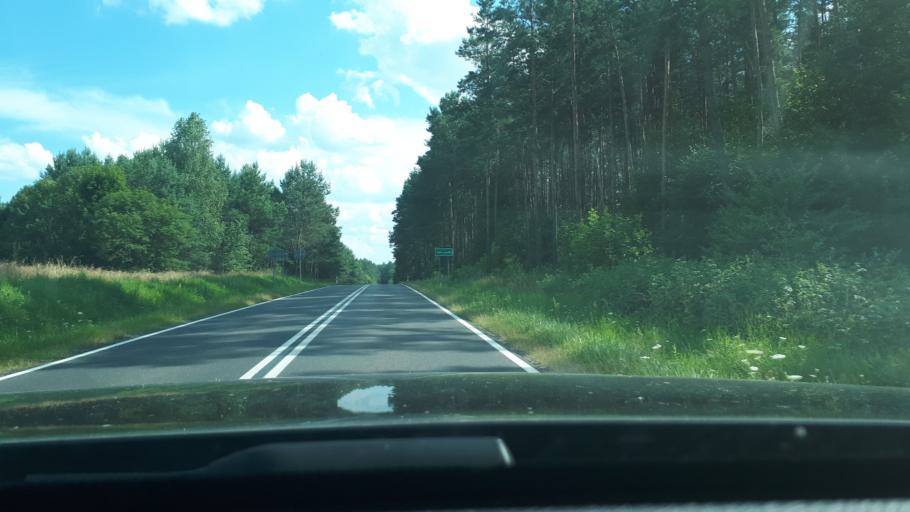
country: PL
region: Warmian-Masurian Voivodeship
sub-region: Powiat olsztynski
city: Stawiguda
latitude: 53.5477
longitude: 20.4187
